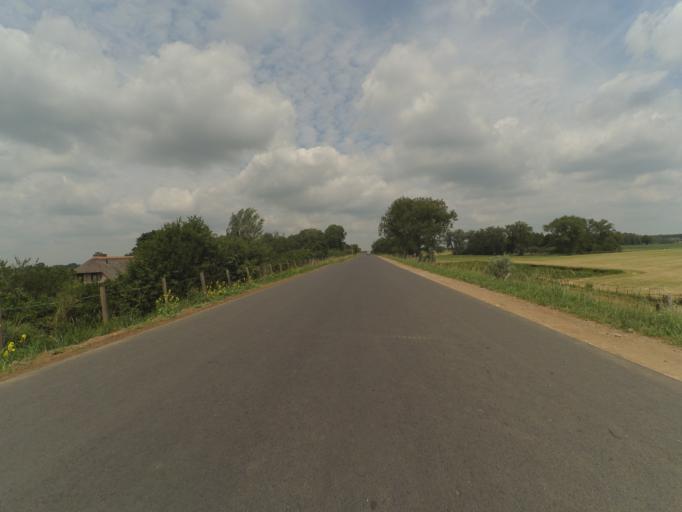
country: NL
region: Gelderland
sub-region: Gemeente Culemborg
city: Culemborg
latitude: 51.9425
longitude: 5.1587
